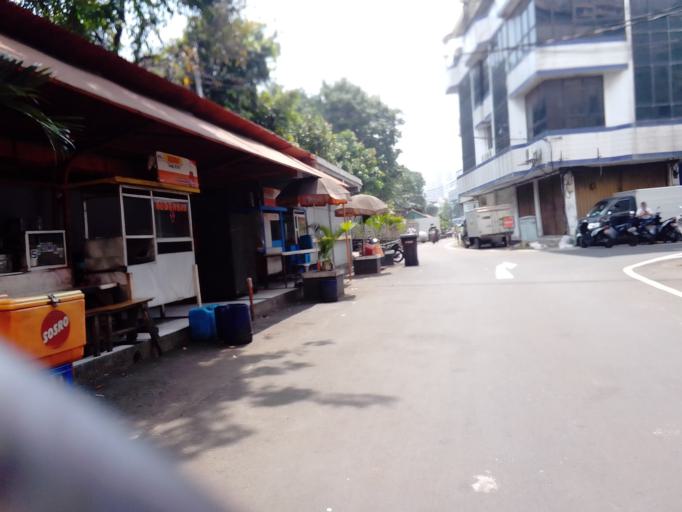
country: ID
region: Jakarta Raya
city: Jakarta
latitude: -6.1380
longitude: 106.8279
